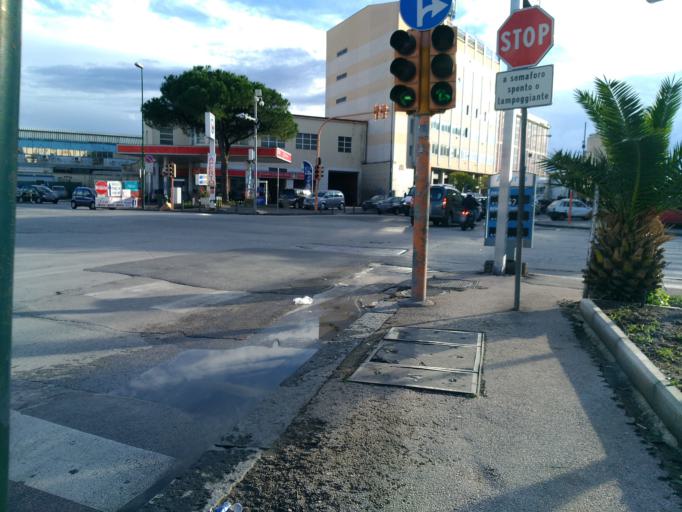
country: IT
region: Campania
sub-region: Provincia di Napoli
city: Napoli
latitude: 40.8499
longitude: 14.2892
